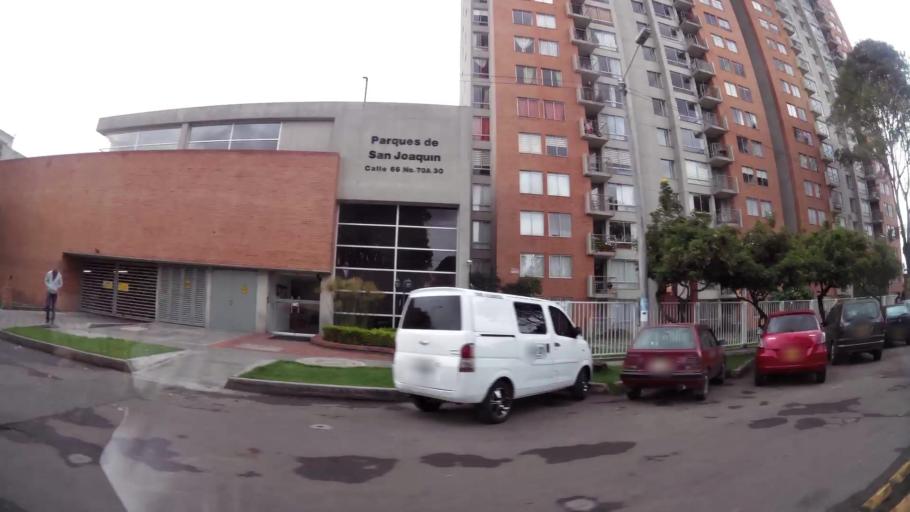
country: CO
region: Bogota D.C.
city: Bogota
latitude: 4.6781
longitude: -74.0969
